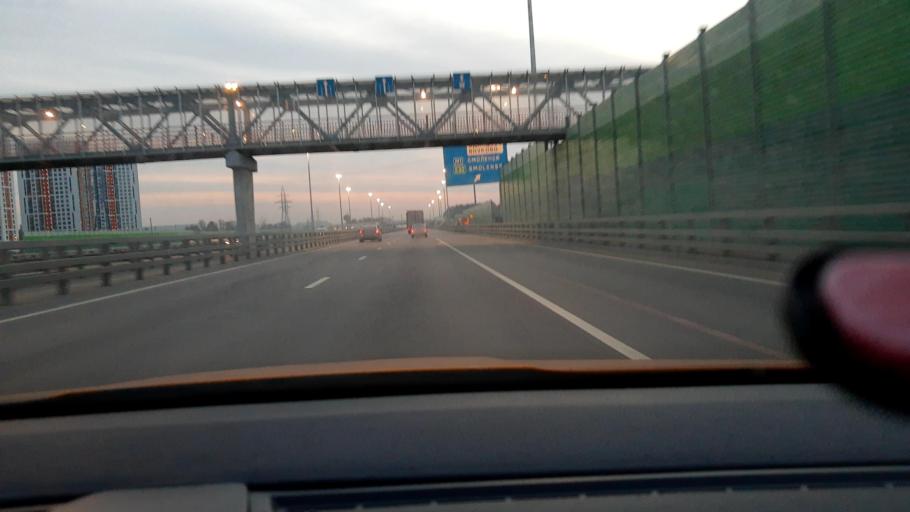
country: RU
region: Moskovskaya
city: Odintsovo
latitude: 55.6504
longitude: 37.2644
